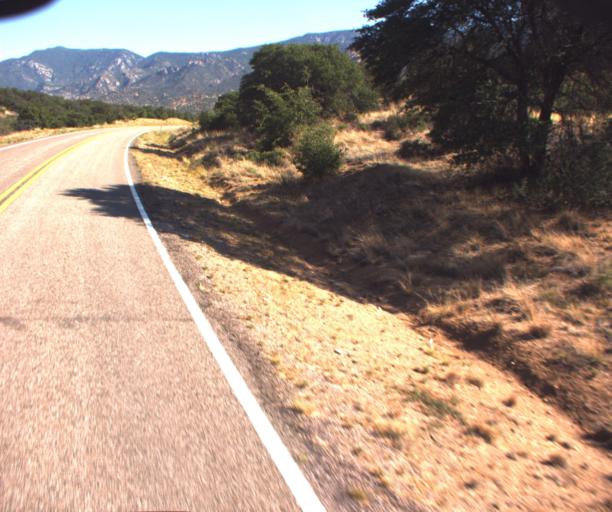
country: US
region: Arizona
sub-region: Graham County
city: Swift Trail Junction
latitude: 32.5852
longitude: -109.8539
